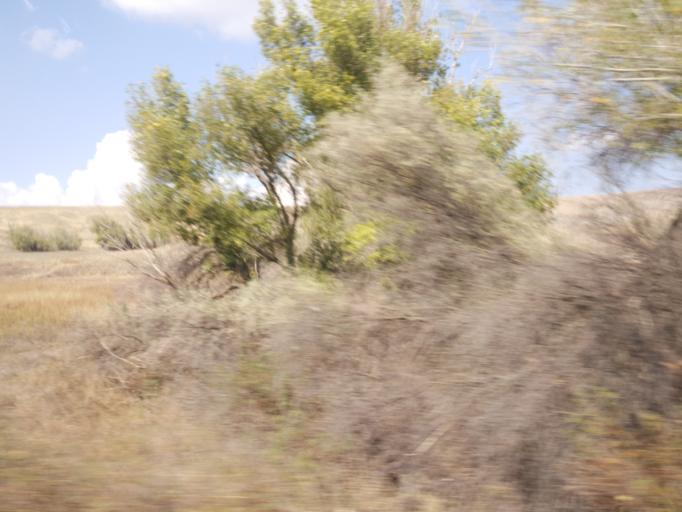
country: TR
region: Corum
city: Bogazkale
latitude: 40.1567
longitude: 34.6081
